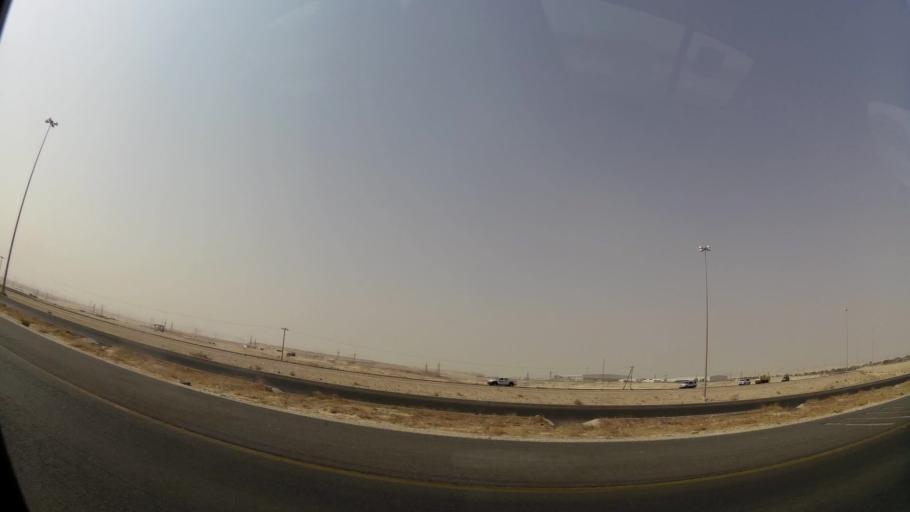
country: KW
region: Muhafazat al Jahra'
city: Al Jahra'
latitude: 29.3340
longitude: 47.6315
